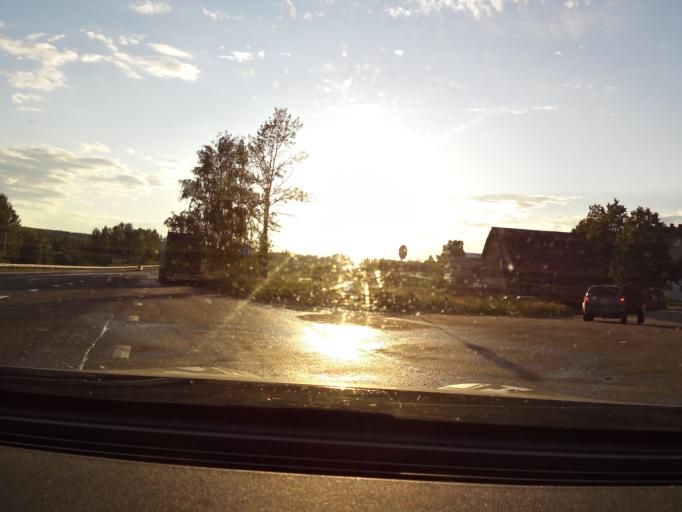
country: RU
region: Vladimir
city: Belaya Rechka
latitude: 56.2815
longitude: 39.4085
